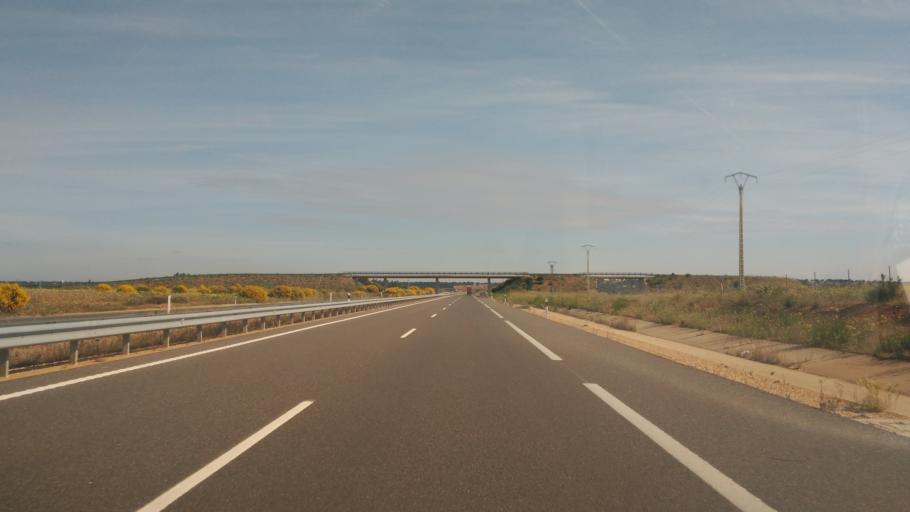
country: ES
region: Castille and Leon
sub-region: Provincia de Salamanca
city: Topas
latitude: 41.1983
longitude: -5.6994
